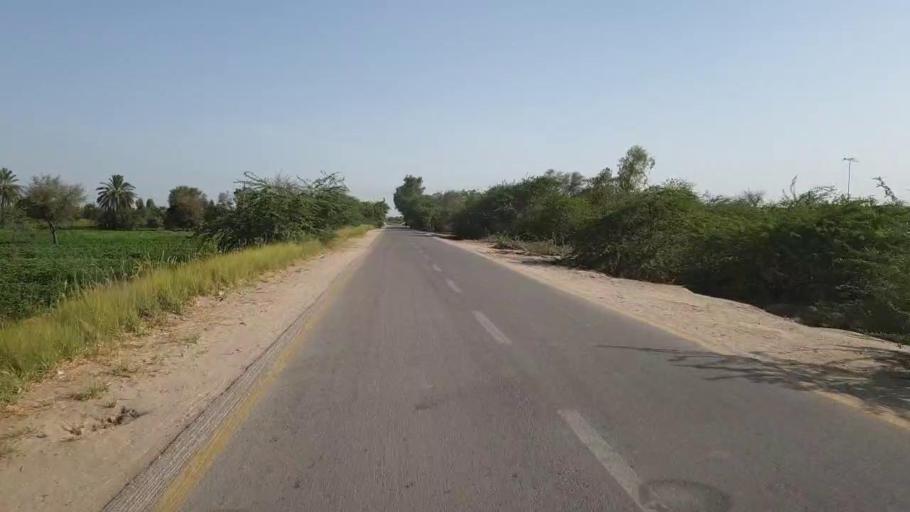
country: PK
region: Sindh
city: Daur
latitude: 26.4636
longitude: 68.4516
